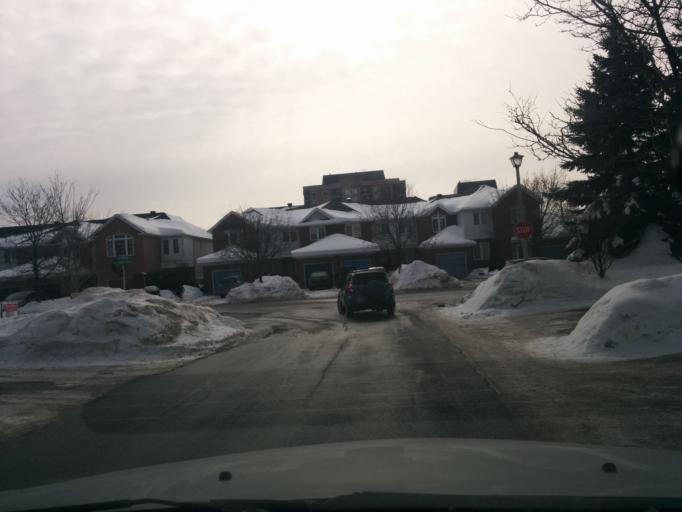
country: CA
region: Ontario
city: Ottawa
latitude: 45.3700
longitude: -75.7349
